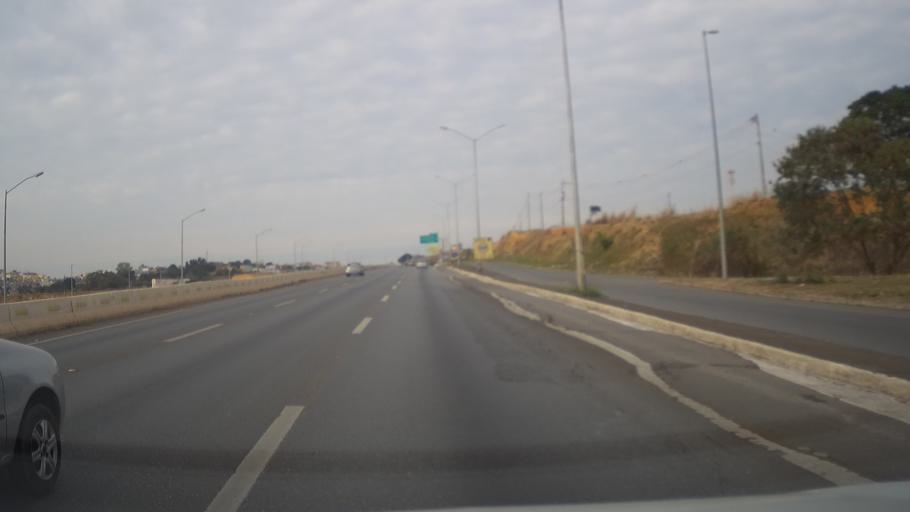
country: BR
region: Minas Gerais
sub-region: Vespasiano
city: Vespasiano
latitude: -19.7393
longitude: -43.9482
